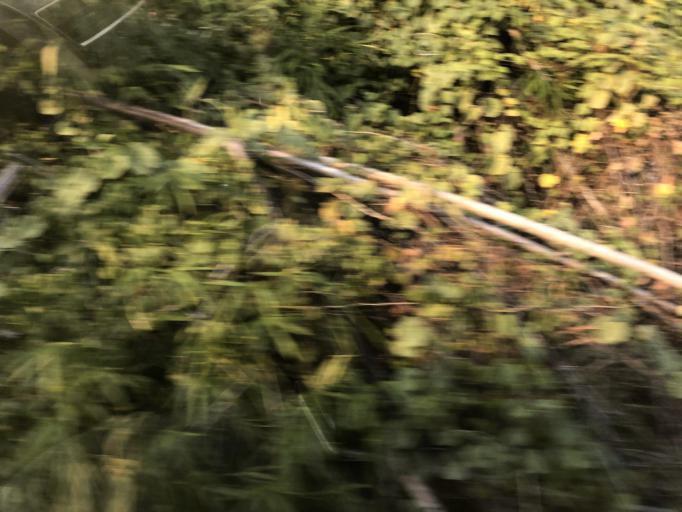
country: TW
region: Taiwan
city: Xinying
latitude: 23.1586
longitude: 120.2725
